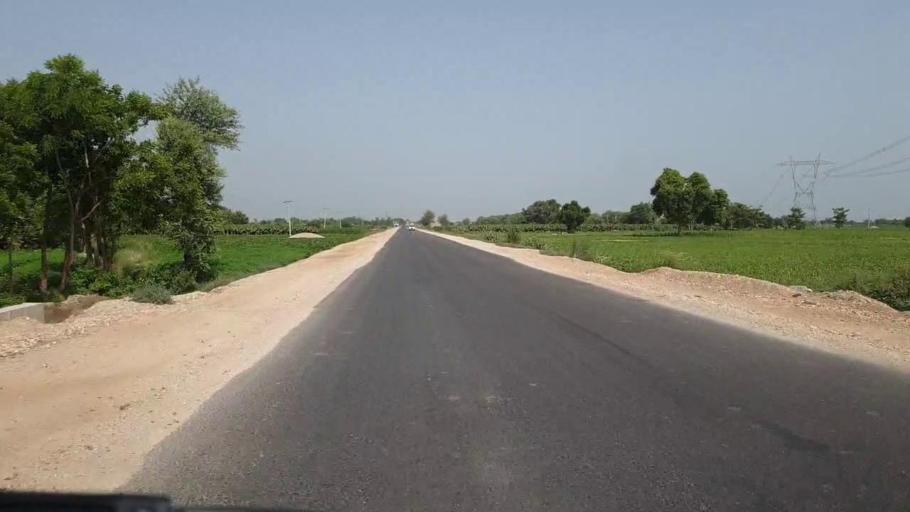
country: PK
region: Sindh
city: Sakrand
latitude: 26.2528
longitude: 68.2032
